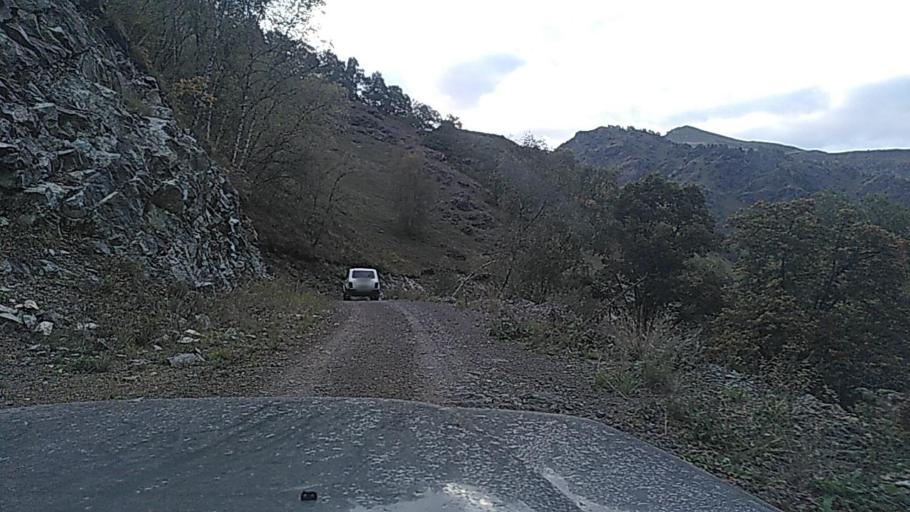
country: RU
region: Kabardino-Balkariya
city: Kamennomostskoye
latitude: 43.7148
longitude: 42.8463
